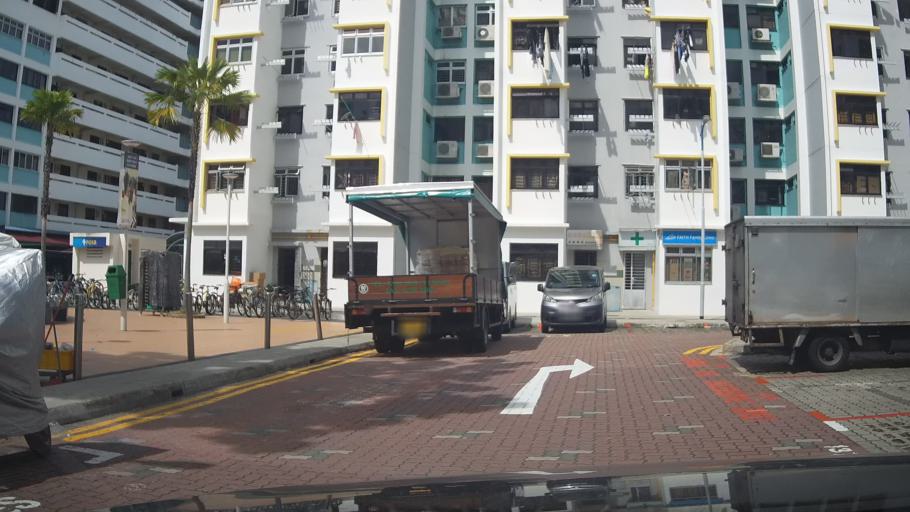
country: SG
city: Singapore
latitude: 1.3060
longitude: 103.9157
